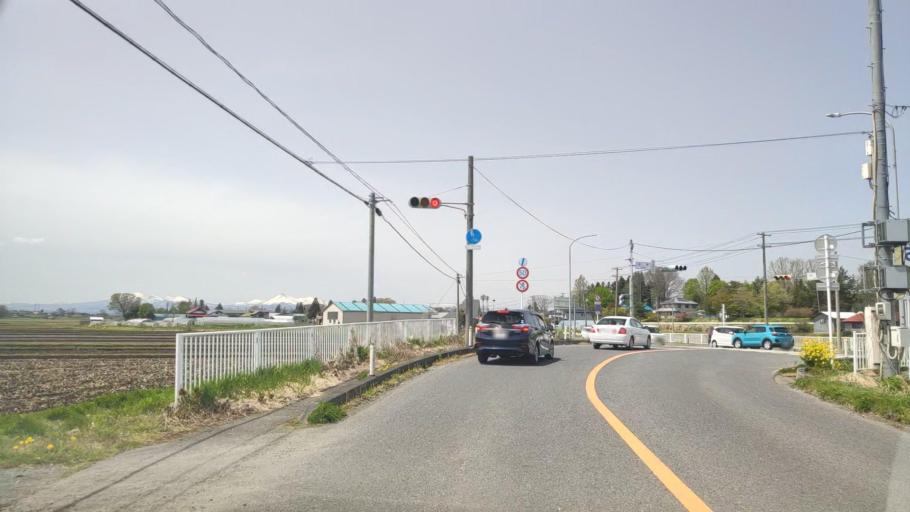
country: JP
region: Aomori
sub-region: Misawa Shi
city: Inuotose
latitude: 40.6049
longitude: 141.2935
